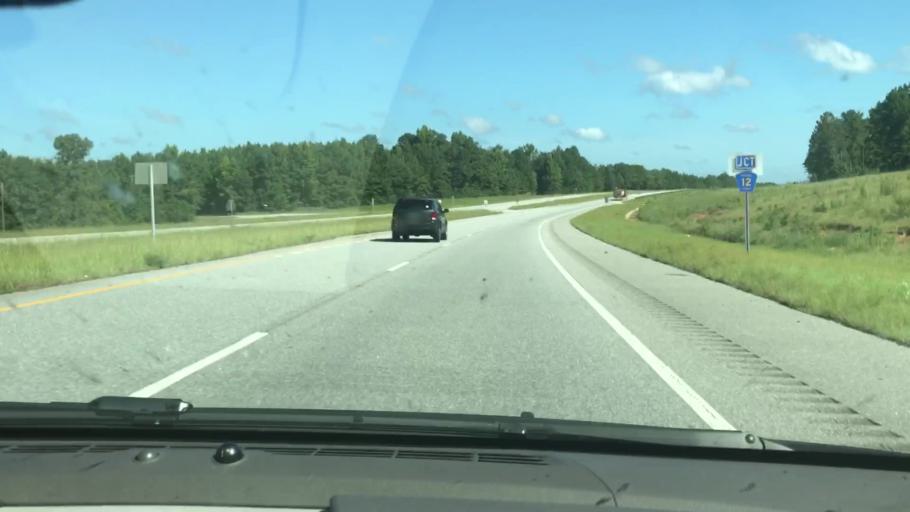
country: US
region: Alabama
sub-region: Barbour County
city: Eufaula
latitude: 32.1558
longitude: -85.1779
